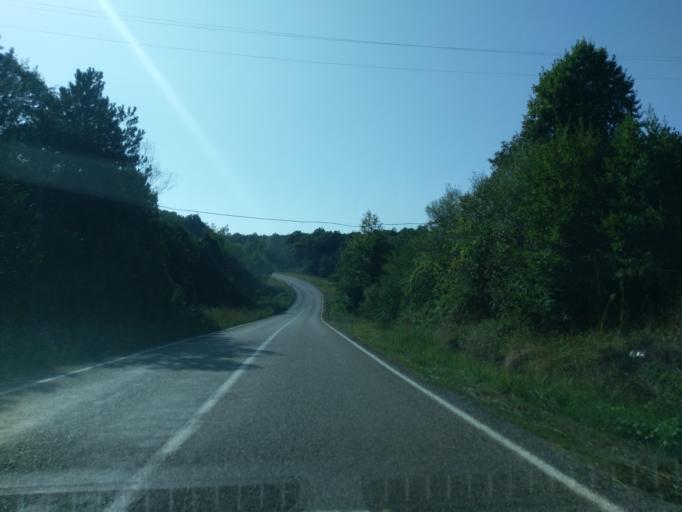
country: TR
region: Sinop
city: Yenikonak
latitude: 41.9465
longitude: 34.7459
